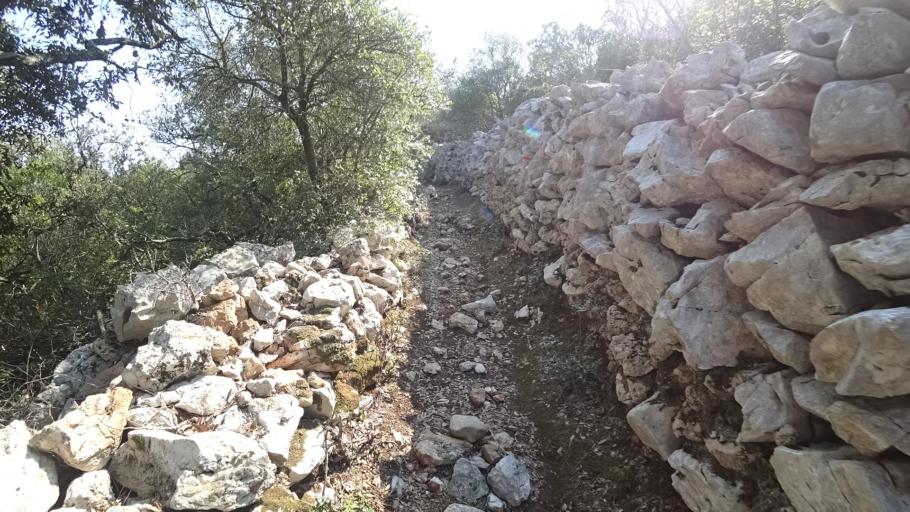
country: HR
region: Primorsko-Goranska
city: Mali Losinj
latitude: 44.4966
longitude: 14.5252
